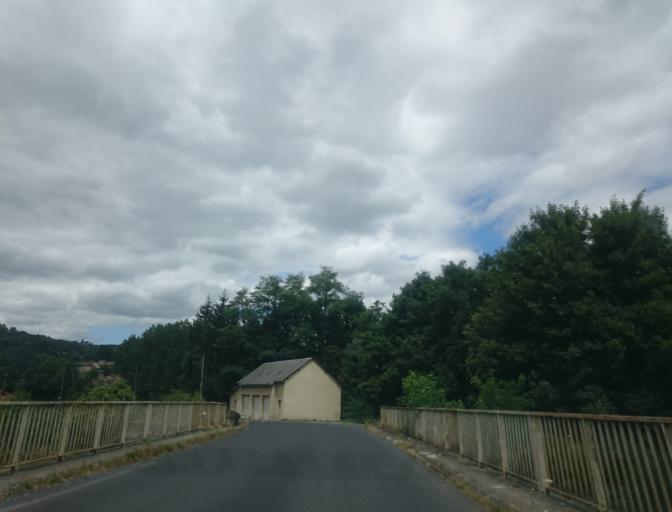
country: FR
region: Auvergne
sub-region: Departement du Cantal
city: Laroquebrou
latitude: 44.9631
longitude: 2.1941
